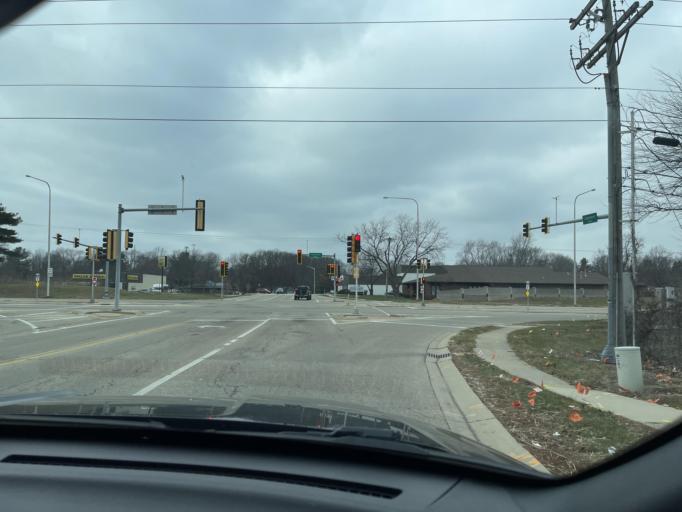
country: US
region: Illinois
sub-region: Sangamon County
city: Leland Grove
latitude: 39.7952
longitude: -89.7059
